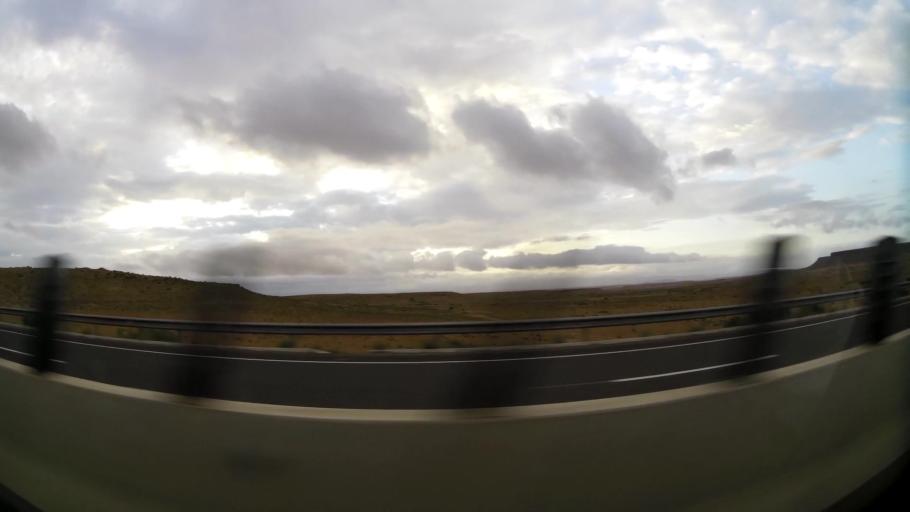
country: MA
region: Oriental
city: Taourirt
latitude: 34.4349
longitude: -3.0899
